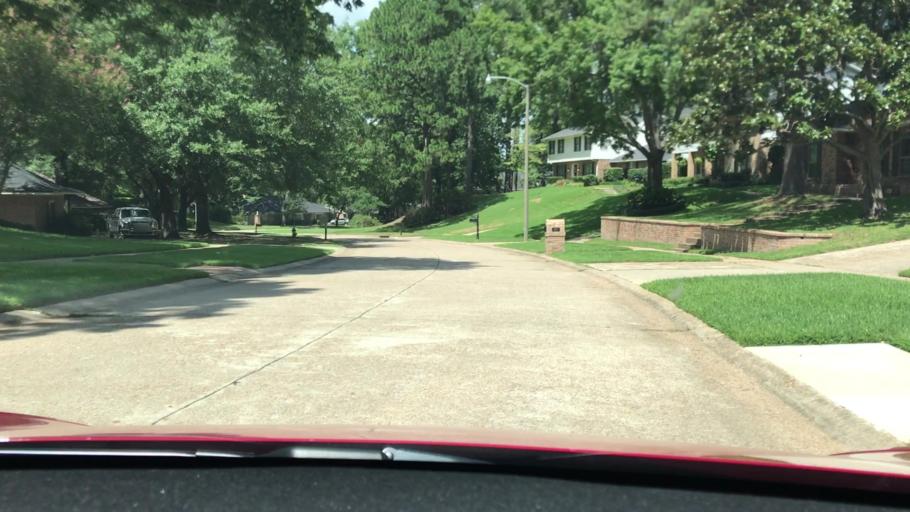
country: US
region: Louisiana
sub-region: Bossier Parish
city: Bossier City
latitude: 32.4249
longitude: -93.7319
